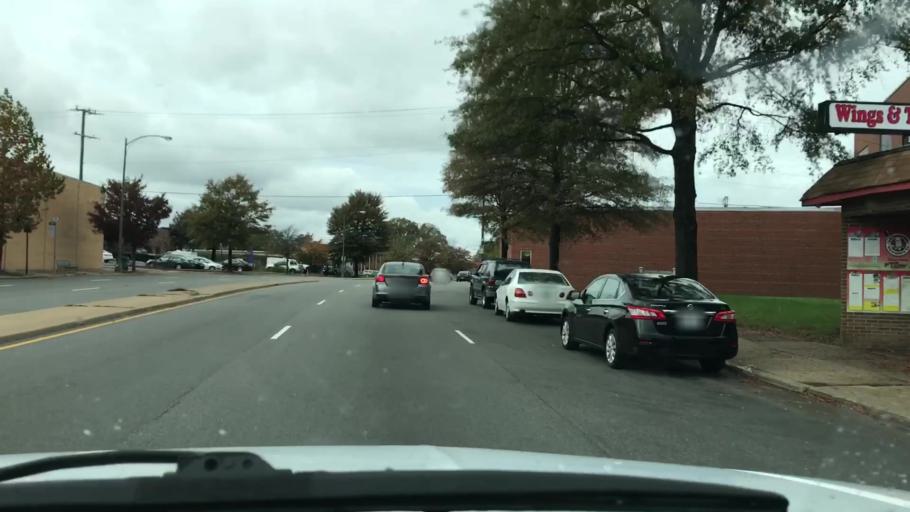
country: US
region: Virginia
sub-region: City of Richmond
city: Richmond
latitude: 37.5570
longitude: -77.4423
